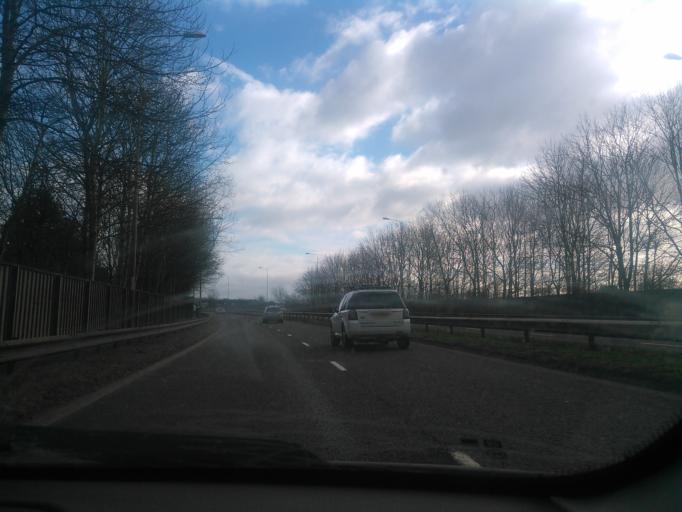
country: GB
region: England
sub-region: Staffordshire
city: Longton
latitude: 52.9627
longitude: -2.0678
